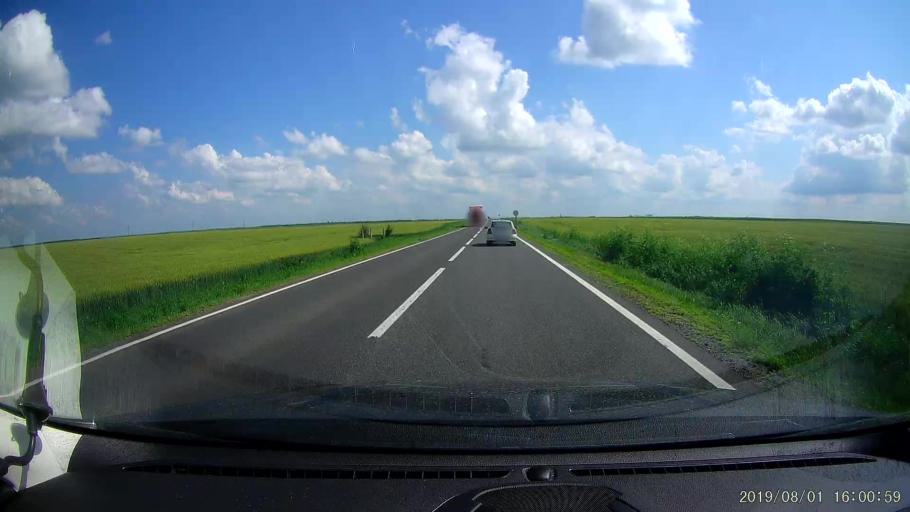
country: RO
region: Ialomita
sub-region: Comuna Ciulnita
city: Ciulnita
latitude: 44.5165
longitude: 27.3896
